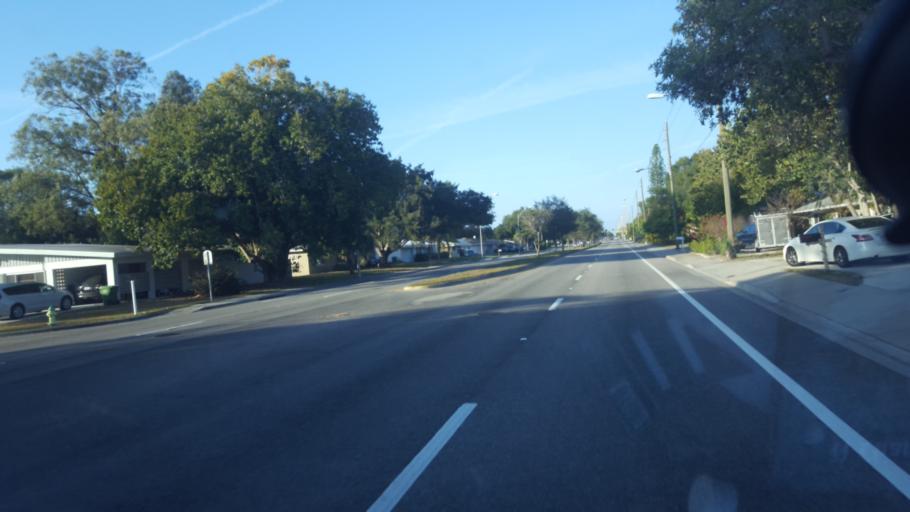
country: US
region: Florida
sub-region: Sarasota County
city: Southgate
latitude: 27.3120
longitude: -82.5140
